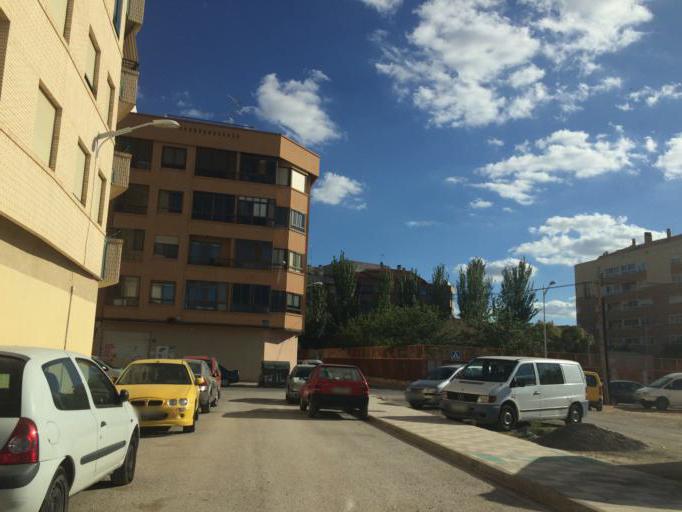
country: ES
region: Castille-La Mancha
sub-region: Provincia de Albacete
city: Albacete
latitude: 38.9945
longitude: -1.8769
